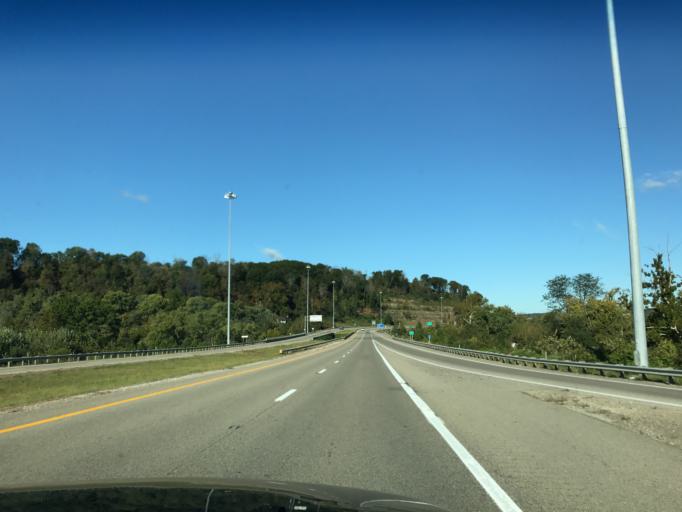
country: US
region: West Virginia
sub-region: Wood County
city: Parkersburg
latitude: 39.2587
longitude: -81.5583
